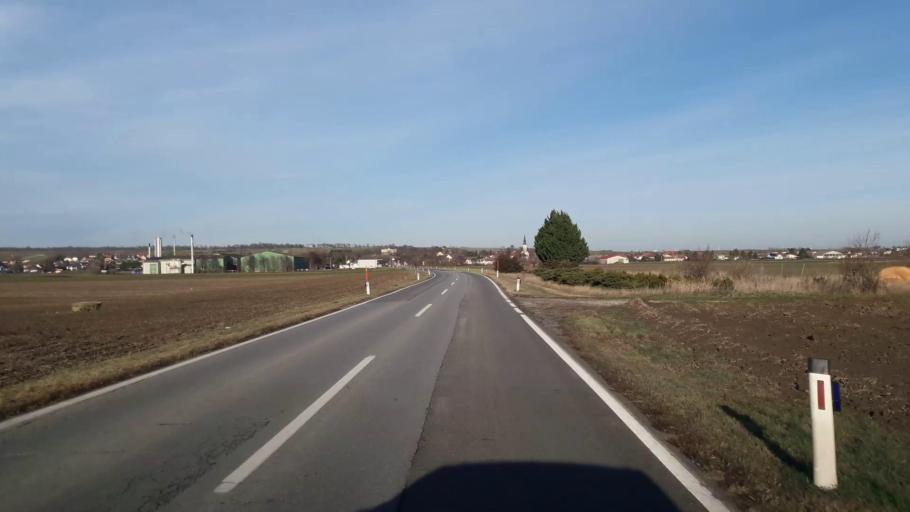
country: AT
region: Lower Austria
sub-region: Politischer Bezirk Mistelbach
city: Bockfliess
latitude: 48.3501
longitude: 16.5986
